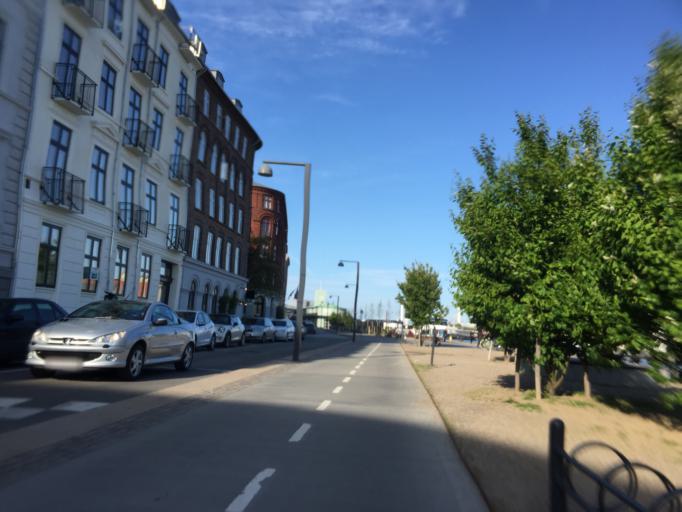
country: DK
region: Capital Region
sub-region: Kobenhavn
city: Christianshavn
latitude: 55.6766
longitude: 12.5889
